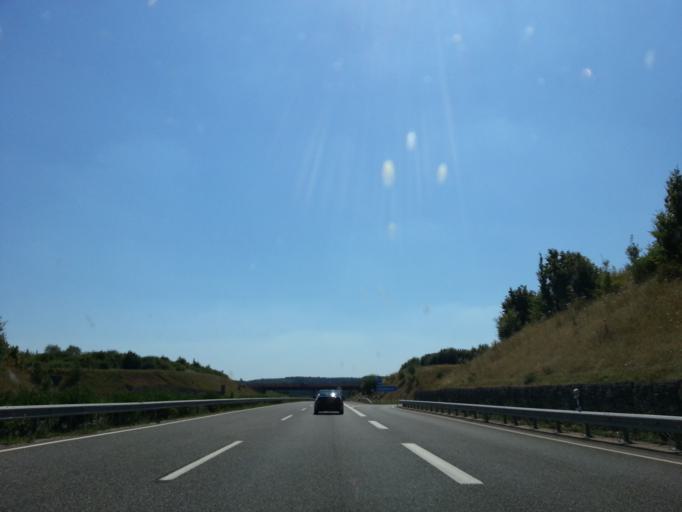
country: DE
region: Rheinland-Pfalz
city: Landscheid
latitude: 49.9917
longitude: 6.7803
